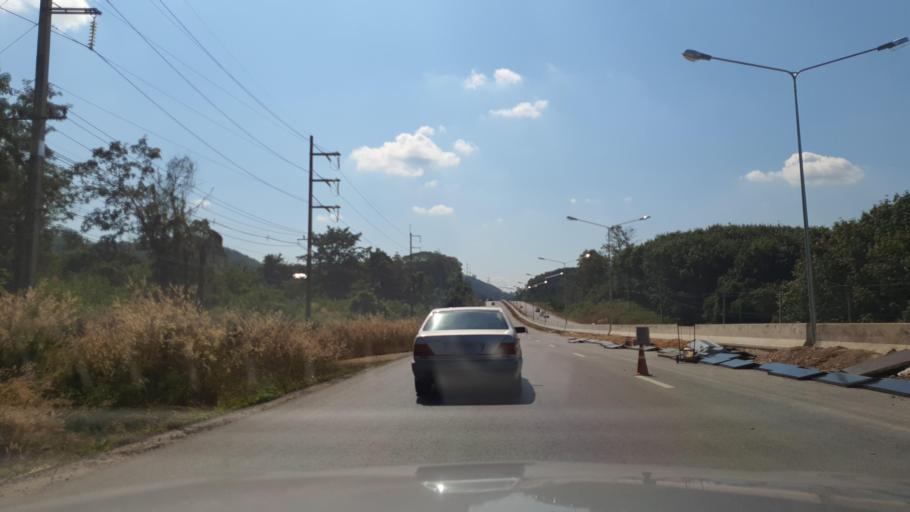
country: TH
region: Nan
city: Nan
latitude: 18.9157
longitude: 100.7639
